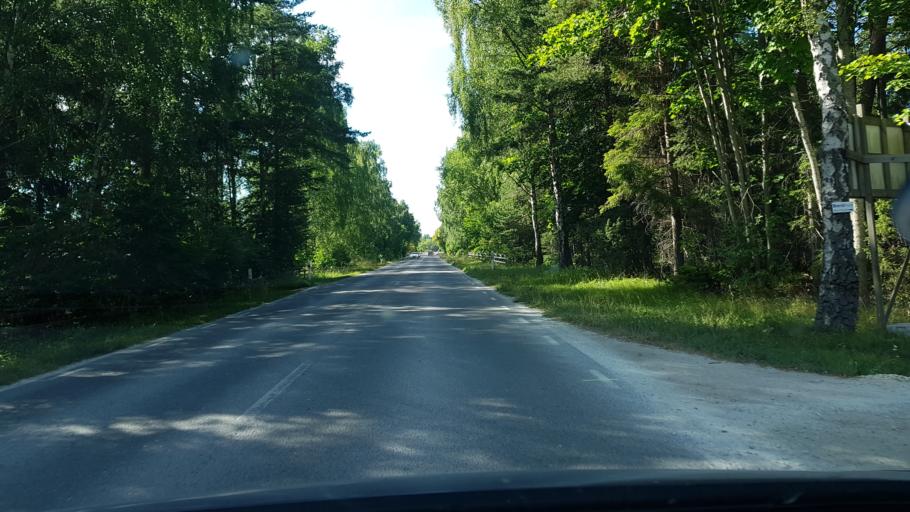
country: SE
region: Gotland
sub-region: Gotland
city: Klintehamn
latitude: 57.4068
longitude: 18.1704
